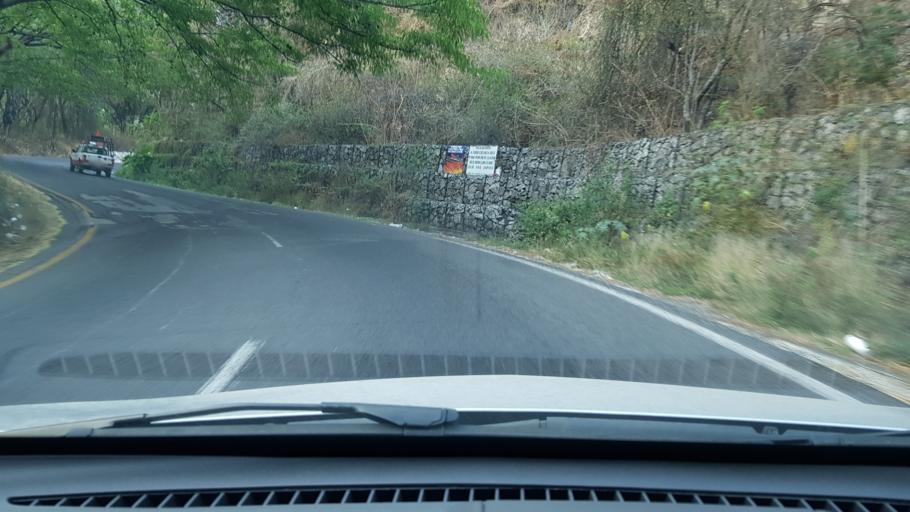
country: MX
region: Morelos
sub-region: Jiutepec
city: Independencia
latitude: 18.8763
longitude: -99.1204
